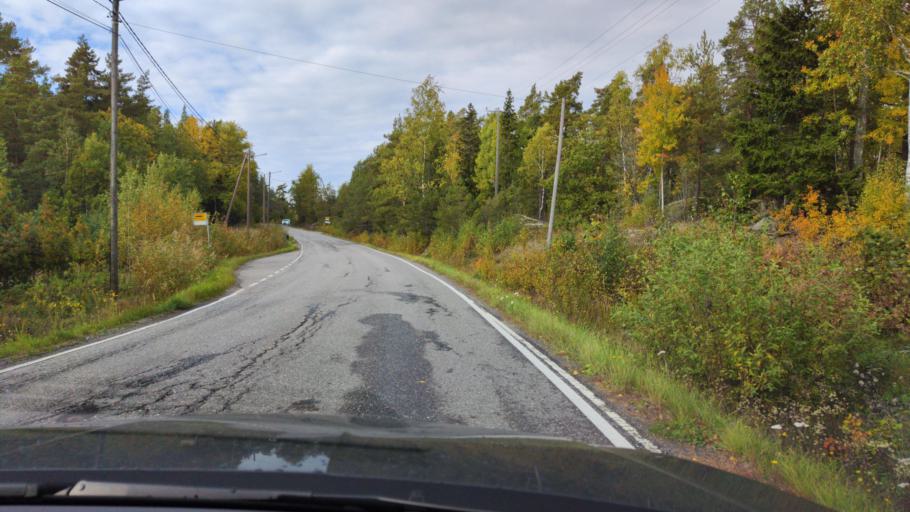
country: FI
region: Varsinais-Suomi
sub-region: Aboland-Turunmaa
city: Pargas
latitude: 60.3535
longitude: 22.1792
